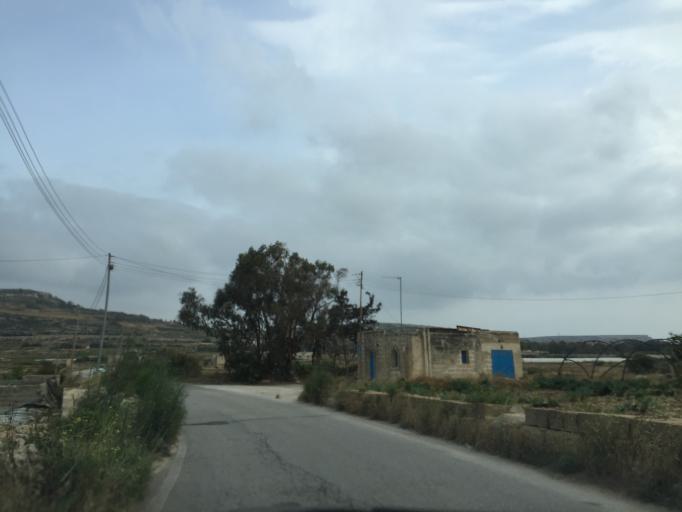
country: MT
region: Il-Mellieha
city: Mellieha
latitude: 35.9376
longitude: 14.3506
